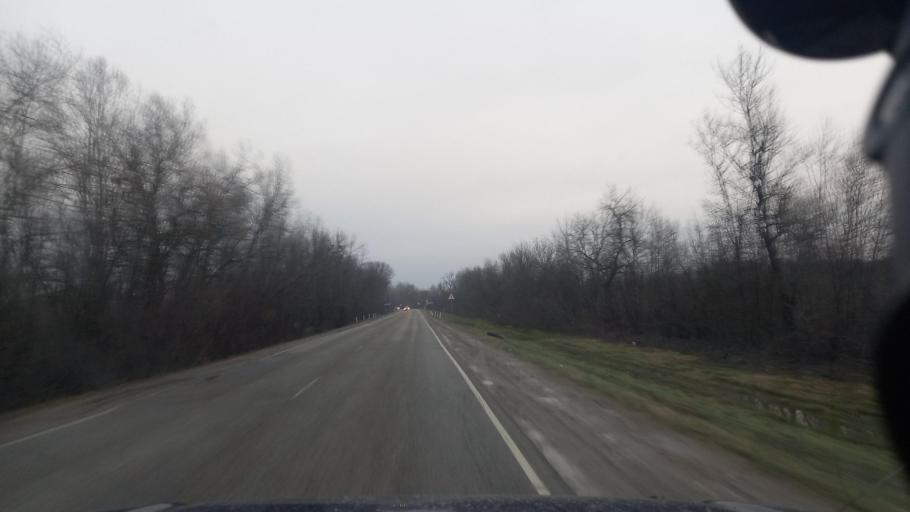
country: RU
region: Krasnodarskiy
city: Saratovskaya
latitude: 44.6883
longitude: 39.2168
